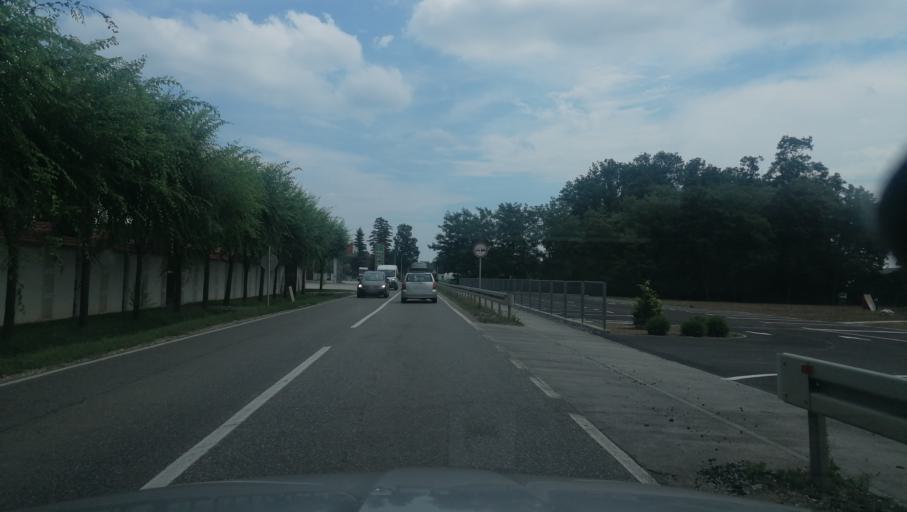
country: BA
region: Republika Srpska
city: Obudovac
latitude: 44.9538
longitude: 18.6422
